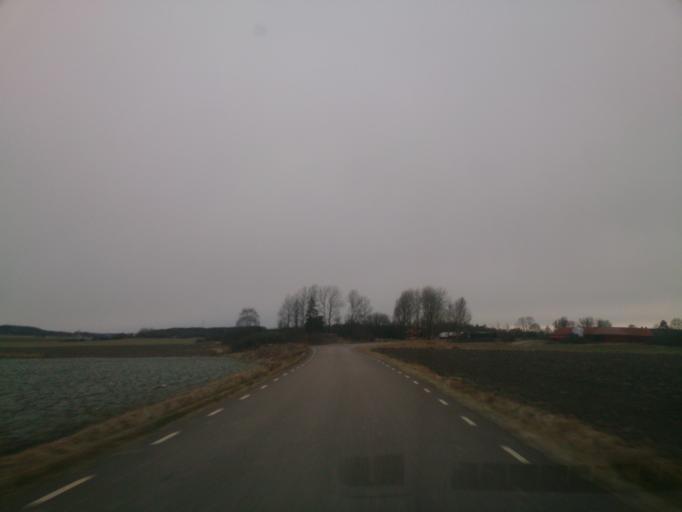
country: SE
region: OEstergoetland
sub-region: Norrkopings Kommun
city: Krokek
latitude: 58.5126
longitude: 16.5256
